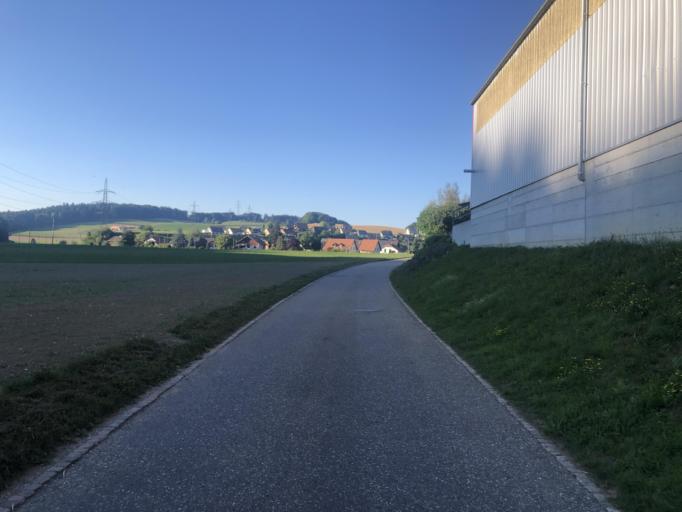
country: CH
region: Bern
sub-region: Emmental District
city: Wynigen
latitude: 47.1021
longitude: 7.6594
